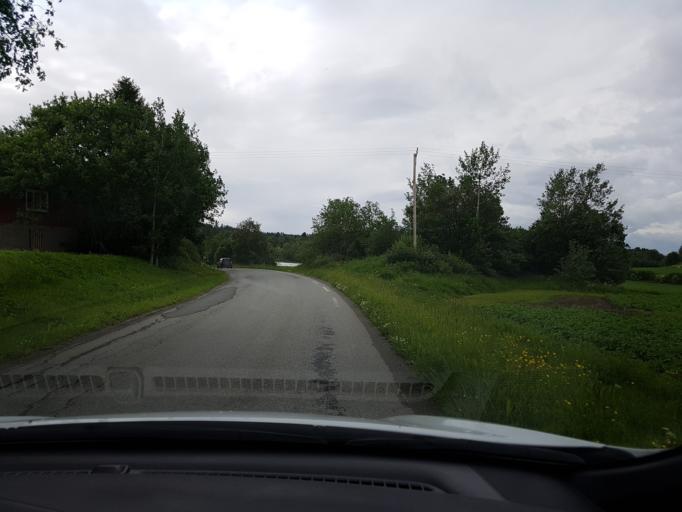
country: NO
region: Nord-Trondelag
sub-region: Frosta
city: Frosta
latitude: 63.6273
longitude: 10.7659
